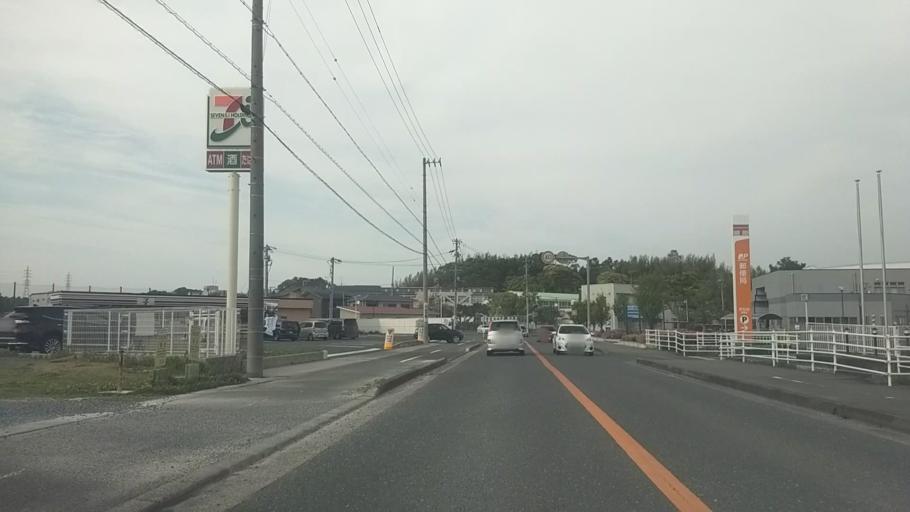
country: JP
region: Shizuoka
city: Hamamatsu
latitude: 34.7429
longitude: 137.6545
